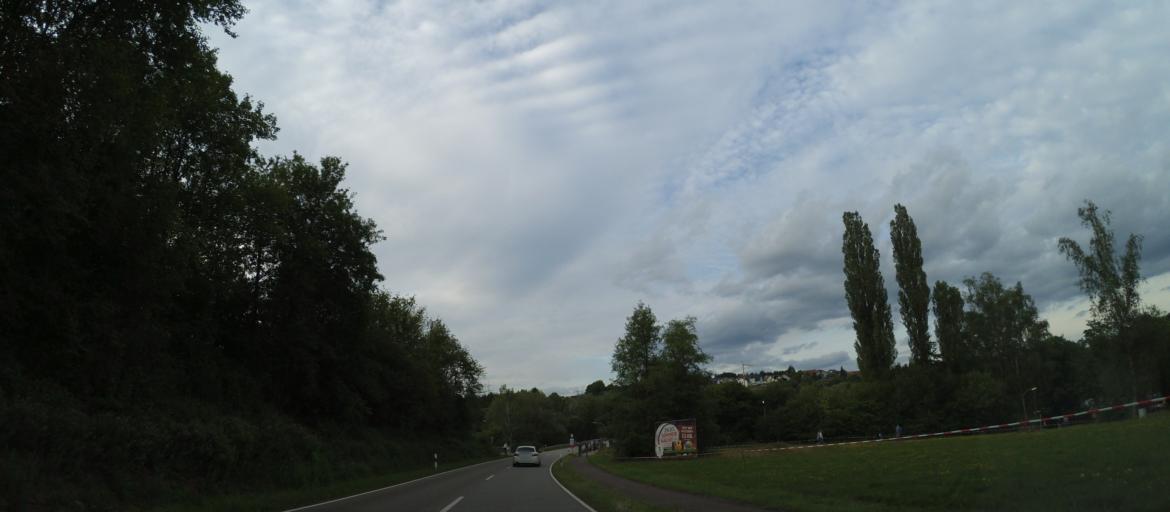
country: DE
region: Rheinland-Pfalz
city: Gries
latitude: 49.4158
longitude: 7.3911
